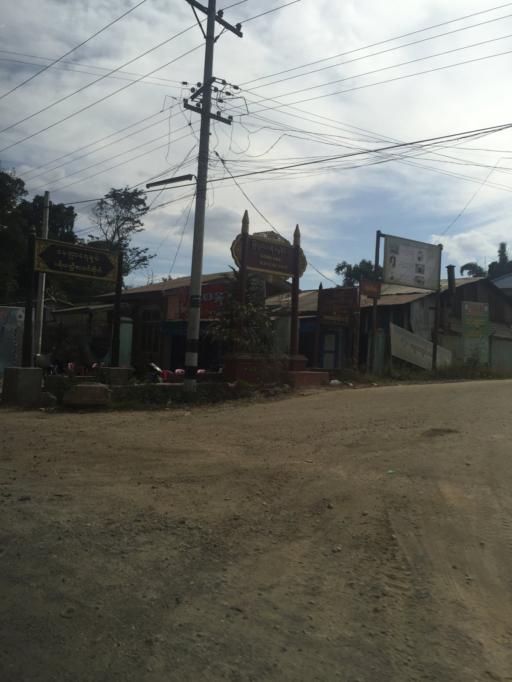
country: MM
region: Mandalay
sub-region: Pyin Oo Lwin District
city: Pyin Oo Lwin
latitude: 22.0419
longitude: 96.5029
